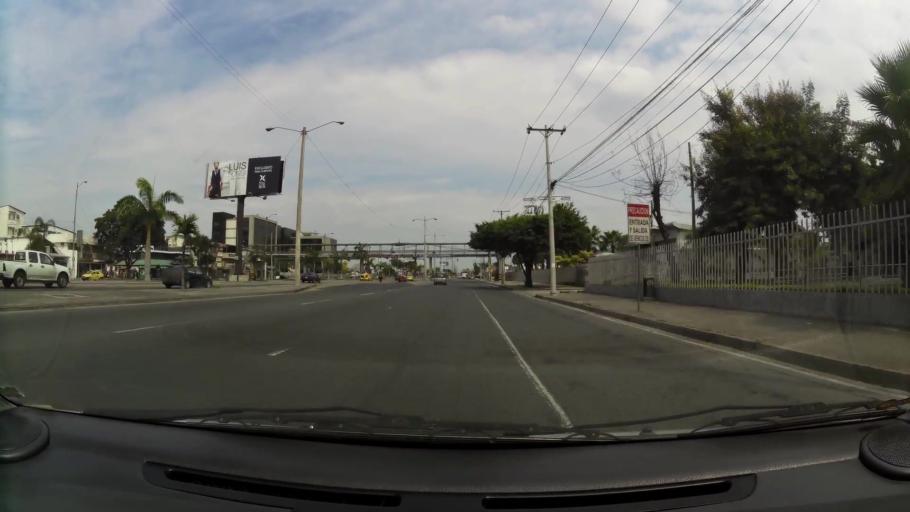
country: EC
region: Guayas
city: Guayaquil
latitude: -2.2423
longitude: -79.8961
